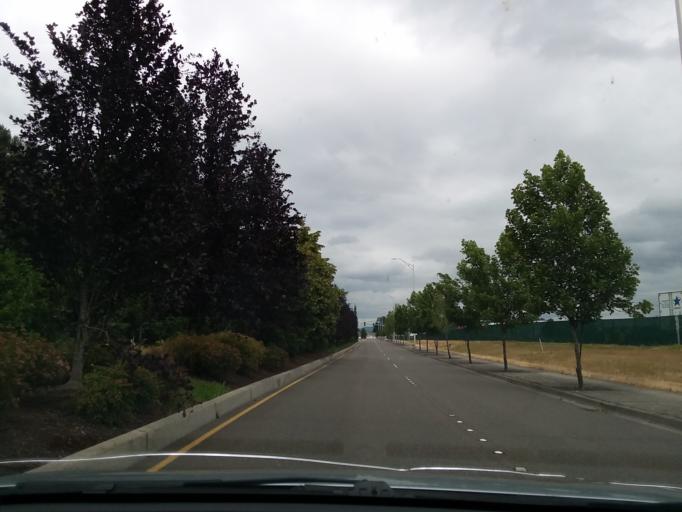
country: US
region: Washington
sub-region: King County
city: SeaTac
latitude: 47.4275
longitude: -122.2697
